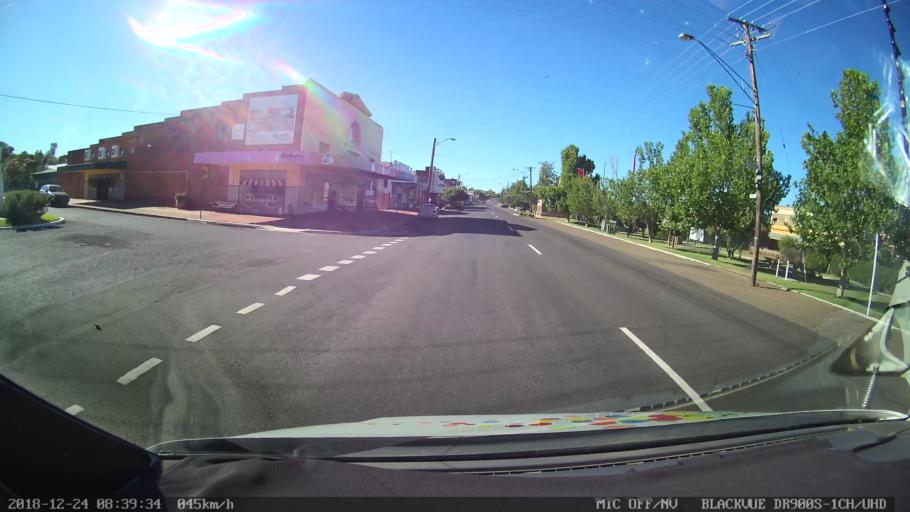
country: AU
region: New South Wales
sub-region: Liverpool Plains
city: Quirindi
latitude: -31.3490
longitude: 150.6472
